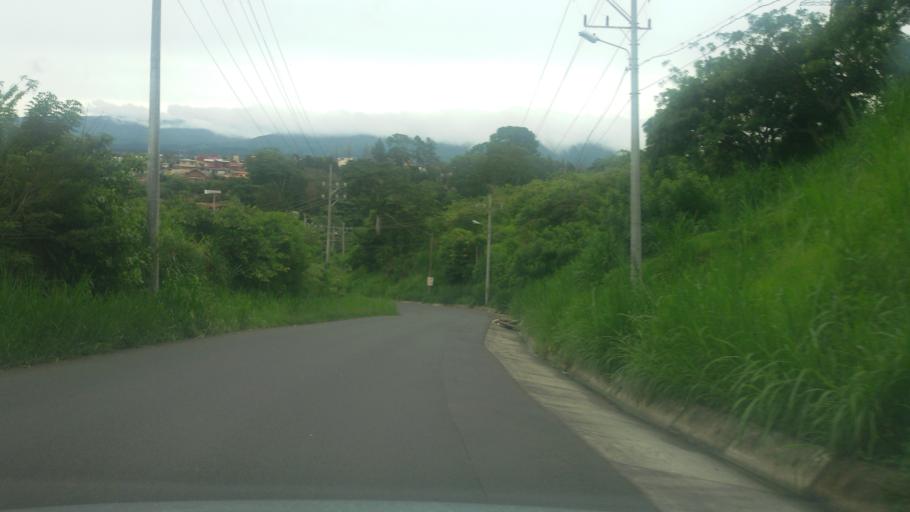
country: CR
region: Heredia
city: Angeles
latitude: 9.9834
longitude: -84.0575
